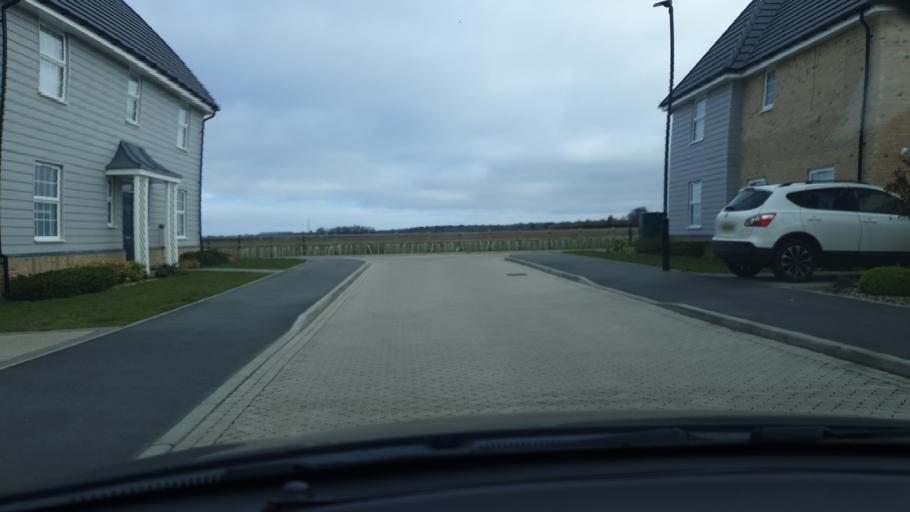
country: GB
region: England
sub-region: Essex
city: Great Bentley
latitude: 51.8593
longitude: 1.0620
